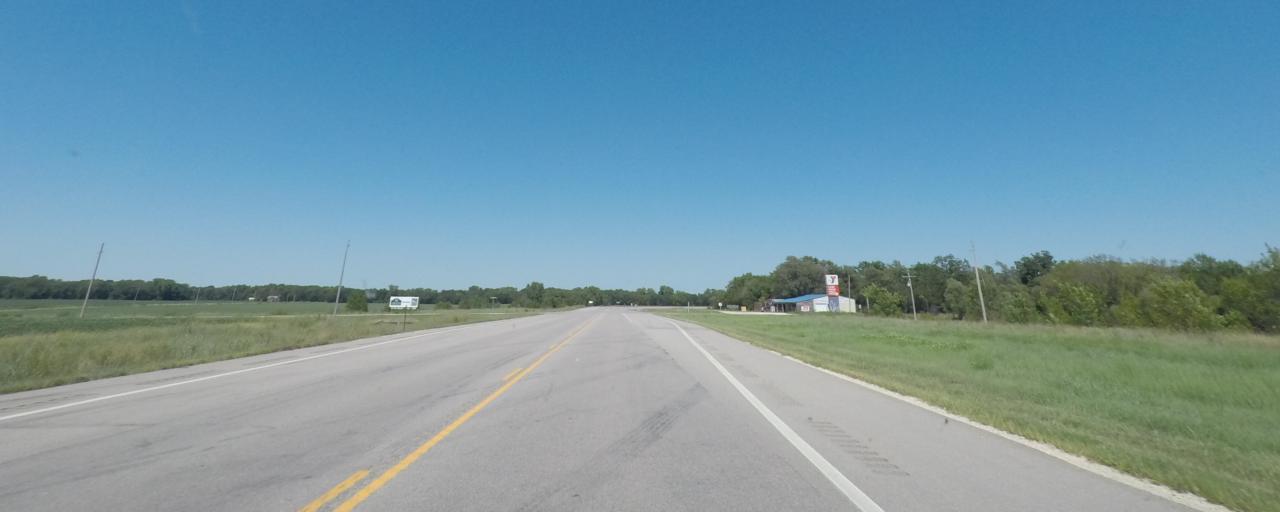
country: US
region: Kansas
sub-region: Chase County
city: Cottonwood Falls
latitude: 38.3723
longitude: -96.6508
